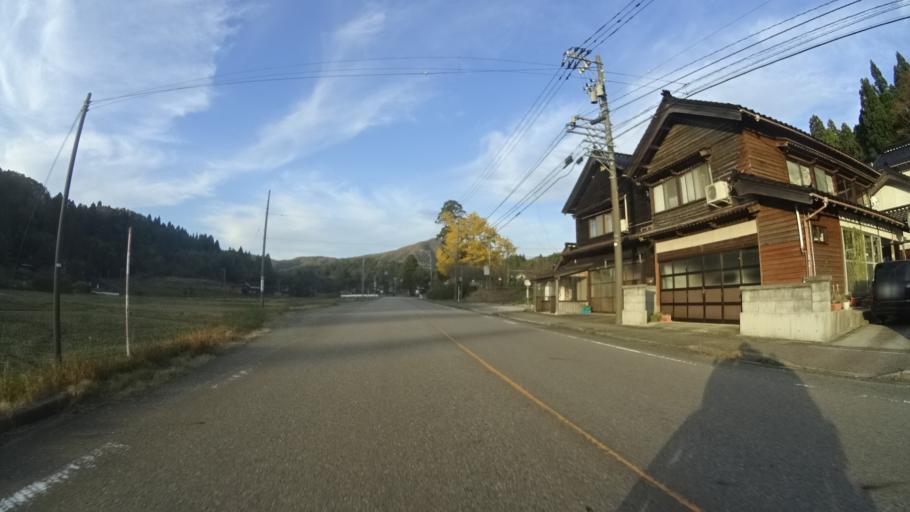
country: JP
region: Ishikawa
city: Nanao
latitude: 37.1889
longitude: 136.7162
